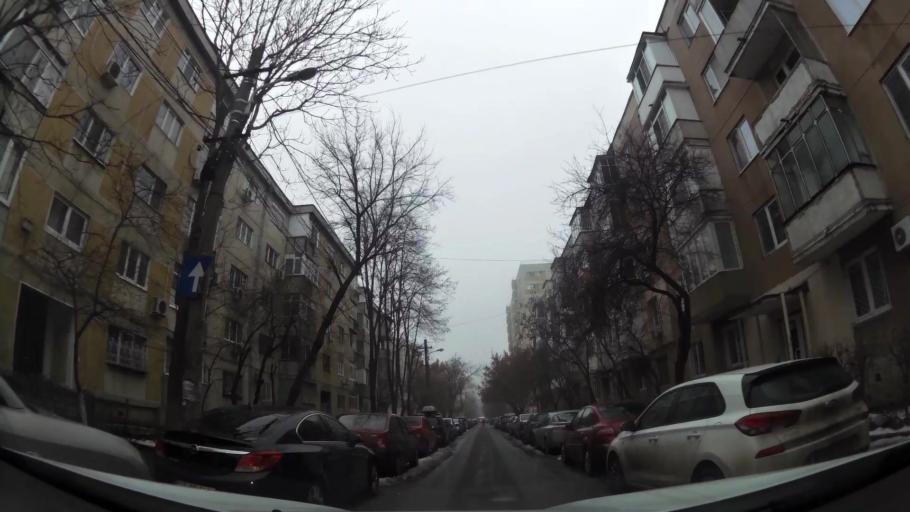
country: RO
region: Ilfov
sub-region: Comuna Chiajna
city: Rosu
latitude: 44.4400
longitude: 26.0238
